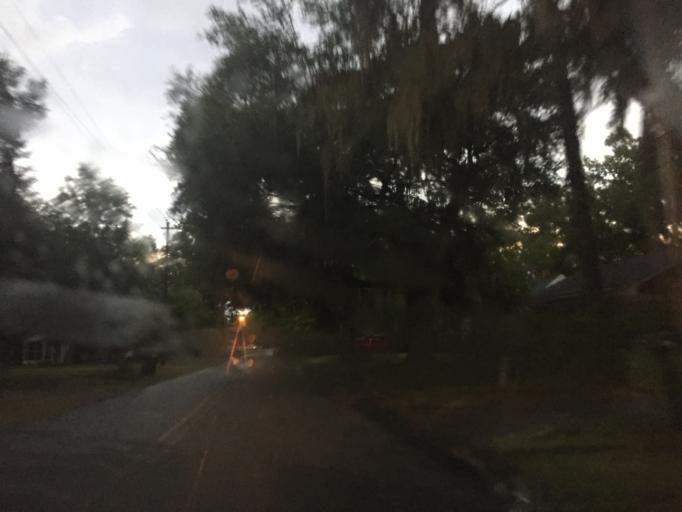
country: US
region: Georgia
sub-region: Liberty County
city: Hinesville
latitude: 31.8439
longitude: -81.5963
